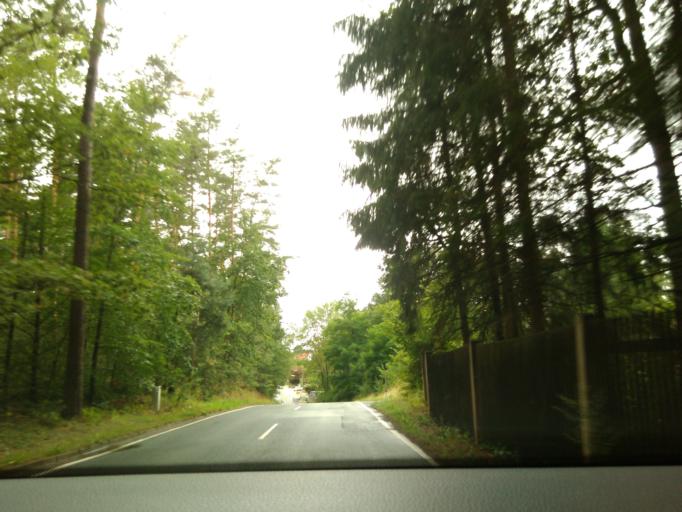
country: DE
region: Bavaria
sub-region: Regierungsbezirk Mittelfranken
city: Cadolzburg
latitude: 49.4576
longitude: 10.8709
